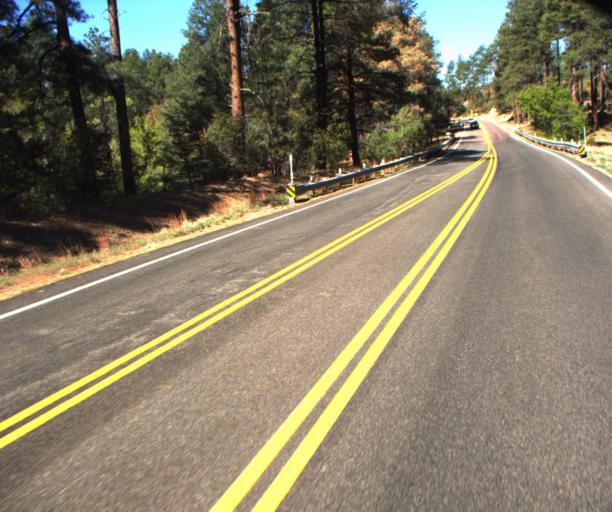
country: US
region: Arizona
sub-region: Yavapai County
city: Prescott
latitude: 34.4959
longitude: -112.4864
